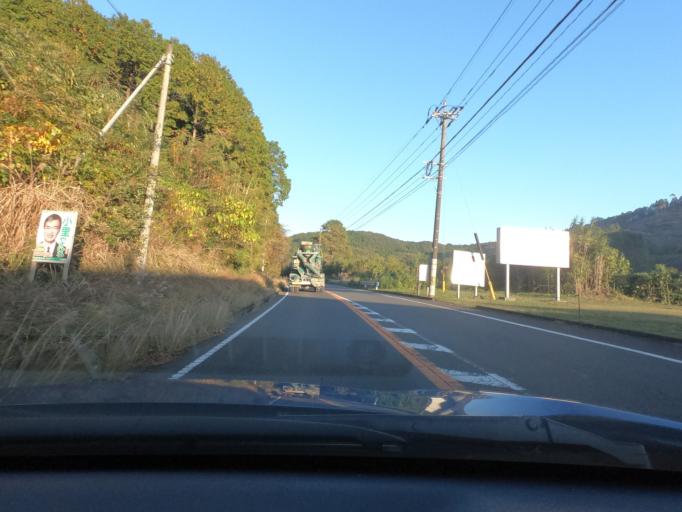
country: JP
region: Kagoshima
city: Satsumasendai
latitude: 31.8041
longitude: 130.3569
